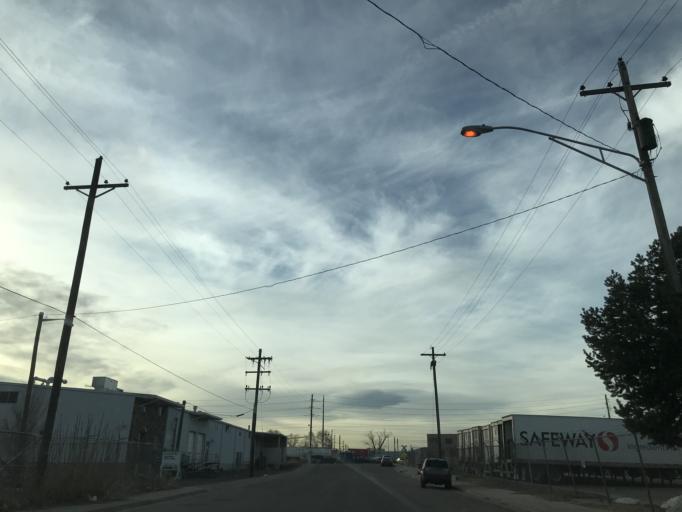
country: US
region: Colorado
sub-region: Adams County
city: Commerce City
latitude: 39.7776
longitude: -104.9270
